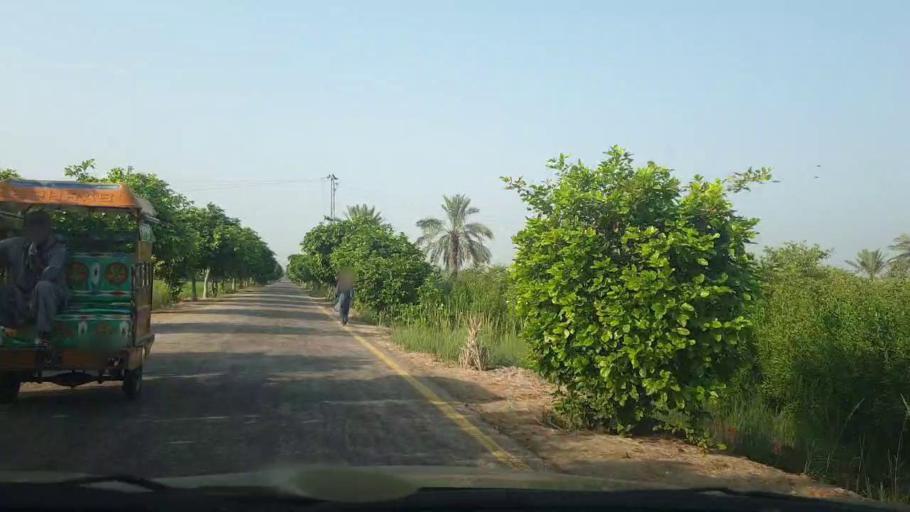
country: PK
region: Sindh
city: Larkana
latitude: 27.5760
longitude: 68.1746
